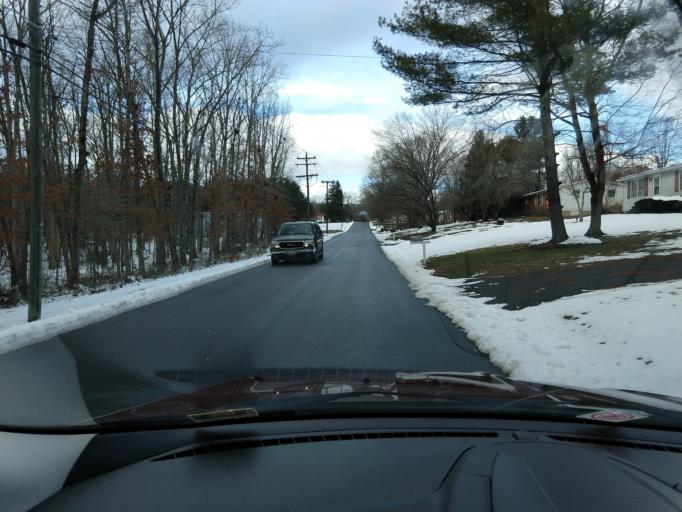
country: US
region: Virginia
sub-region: Alleghany County
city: Clifton Forge
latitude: 37.8209
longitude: -79.8120
